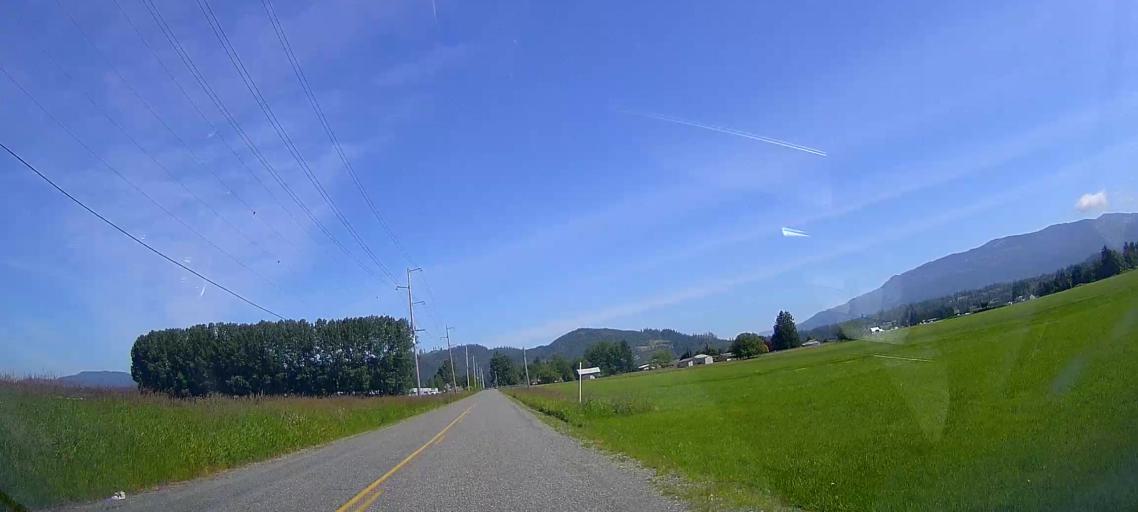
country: US
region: Washington
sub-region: Skagit County
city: Burlington
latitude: 48.5093
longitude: -122.2917
